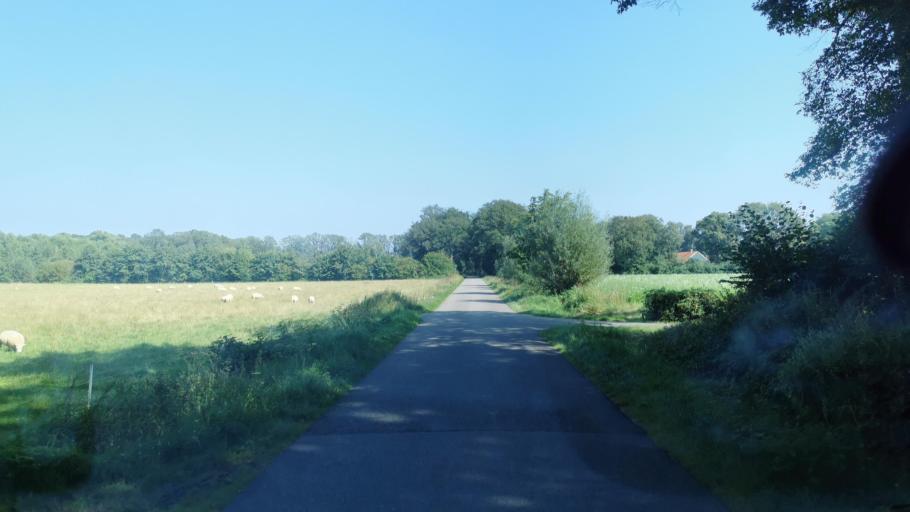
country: NL
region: Overijssel
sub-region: Gemeente Oldenzaal
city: Oldenzaal
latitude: 52.3422
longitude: 6.8971
